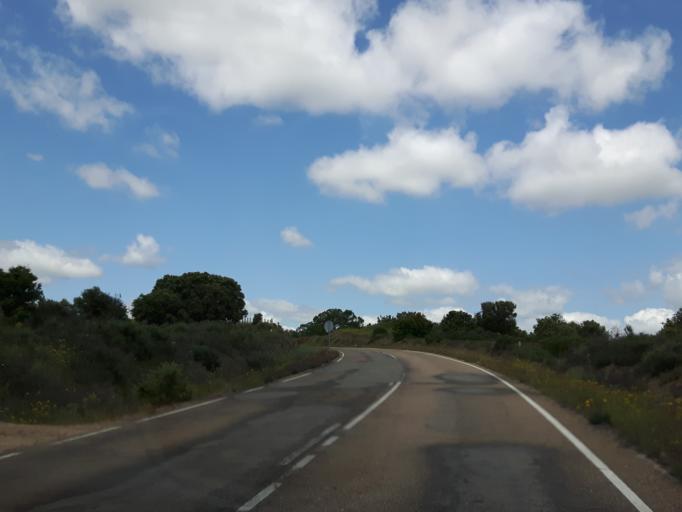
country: ES
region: Castille and Leon
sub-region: Provincia de Salamanca
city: Villar de la Yegua
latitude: 40.7151
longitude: -6.6878
